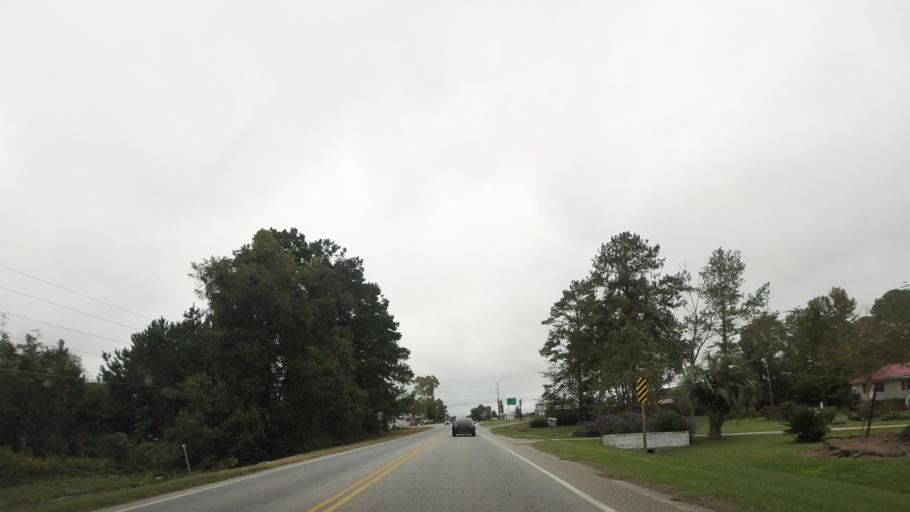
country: US
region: Georgia
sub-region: Berrien County
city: Ray City
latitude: 31.0241
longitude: -83.1979
